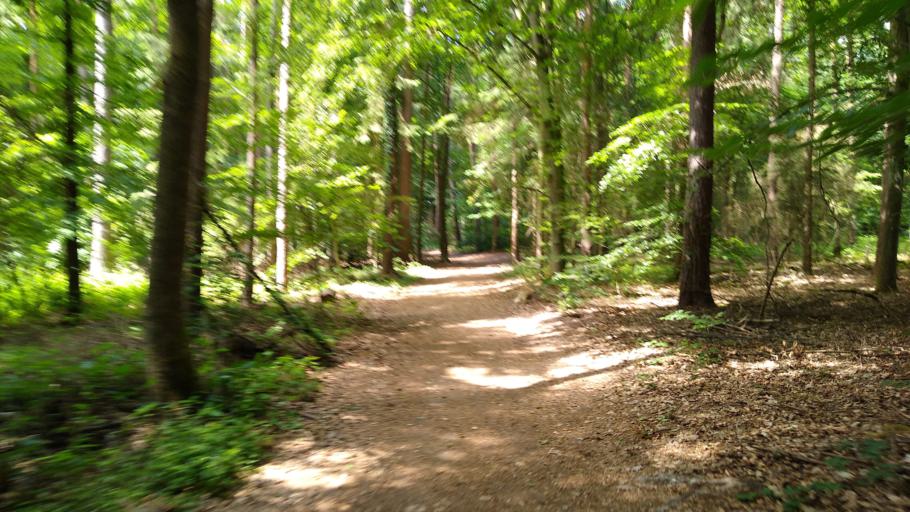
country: DE
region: Bavaria
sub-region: Regierungsbezirk Mittelfranken
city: Seukendorf
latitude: 49.4865
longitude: 10.9056
